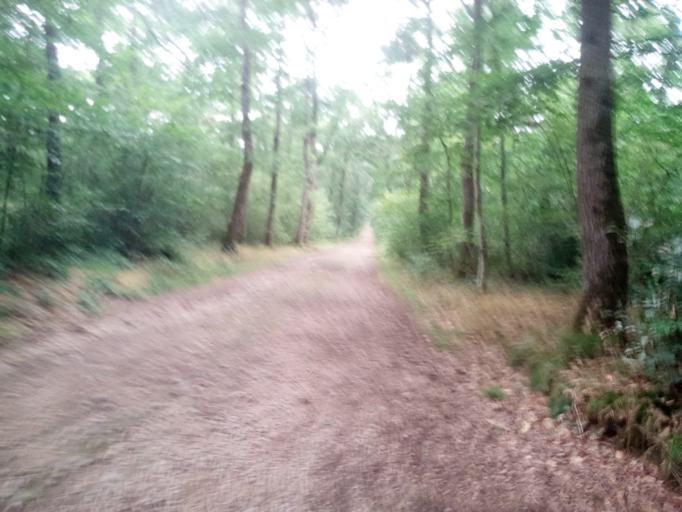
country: FR
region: Lower Normandy
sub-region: Departement du Calvados
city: Clinchamps-sur-Orne
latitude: 49.0462
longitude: -0.4320
